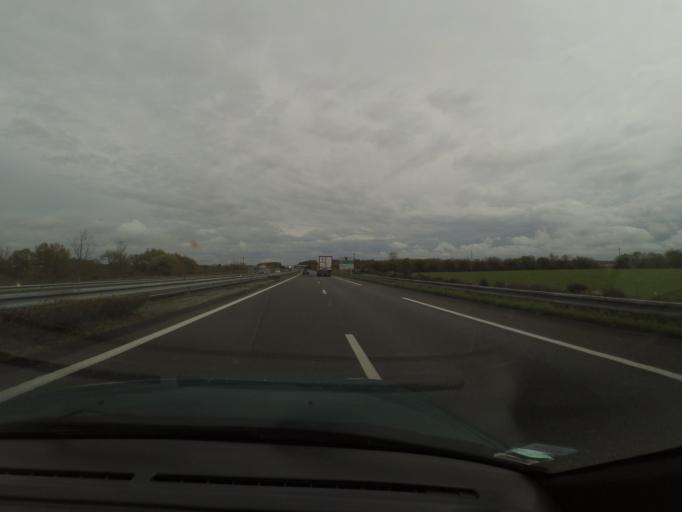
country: FR
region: Pays de la Loire
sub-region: Departement de Maine-et-Loire
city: Saint-Leger-des-Bois
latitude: 47.4544
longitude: -0.7071
